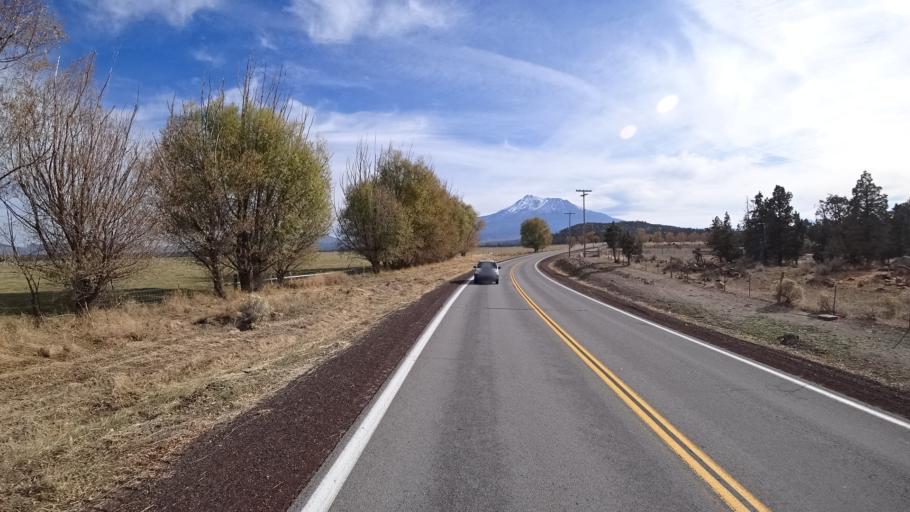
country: US
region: California
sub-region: Siskiyou County
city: Weed
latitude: 41.5487
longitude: -122.3768
